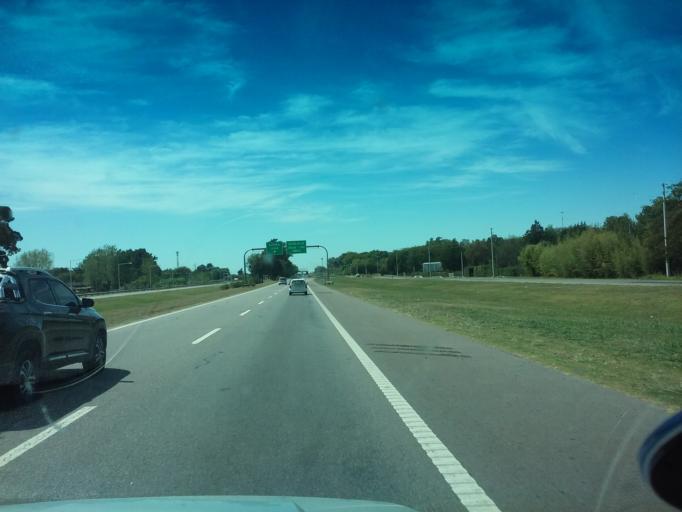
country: AR
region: Buenos Aires
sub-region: Partido de Mercedes
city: Mercedes
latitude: -34.6592
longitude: -59.3694
